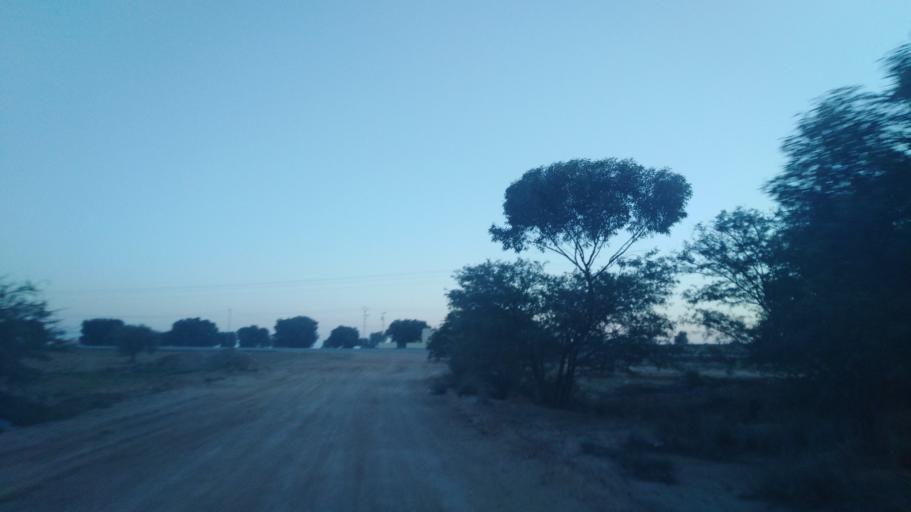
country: TN
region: Safaqis
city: Sfax
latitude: 34.7258
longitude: 10.4471
